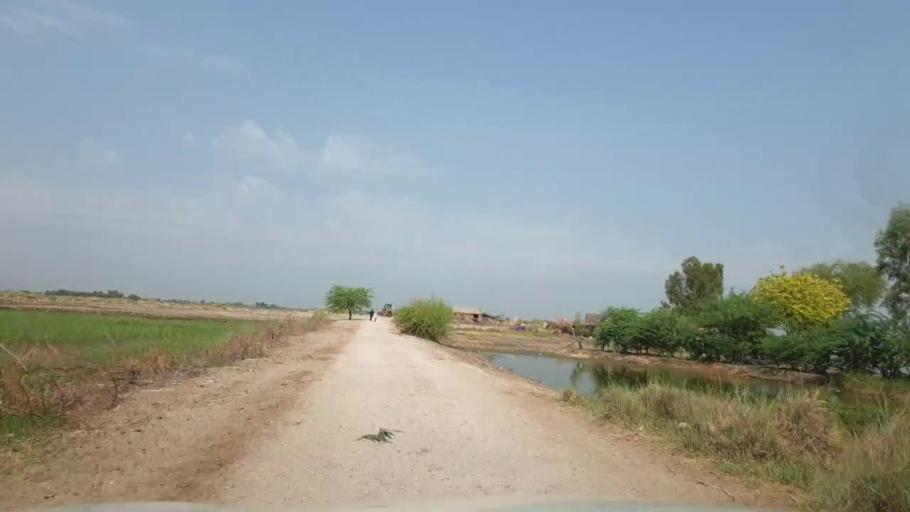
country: PK
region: Sindh
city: Ratodero
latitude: 27.8380
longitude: 68.2602
